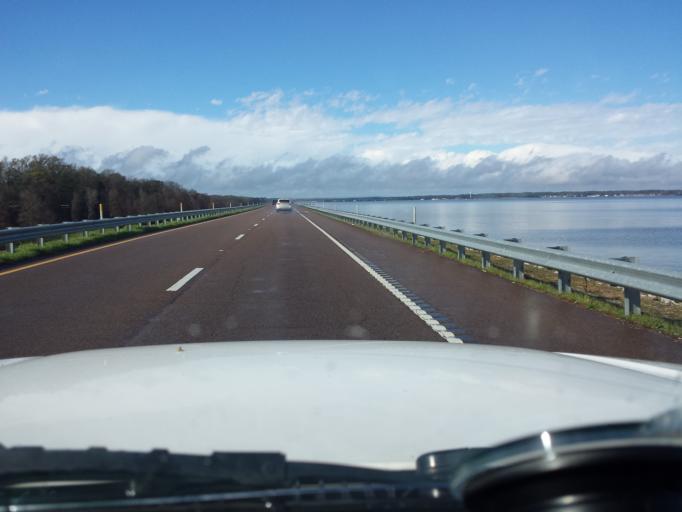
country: US
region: Mississippi
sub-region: Madison County
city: Ridgeland
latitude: 32.3909
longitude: -90.0542
